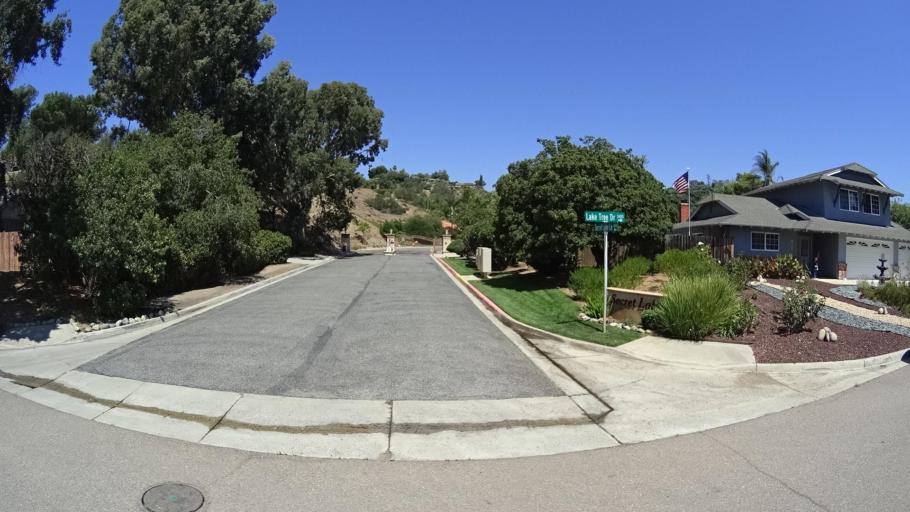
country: US
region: California
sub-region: San Diego County
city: Bonsall
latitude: 33.3415
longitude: -117.1889
